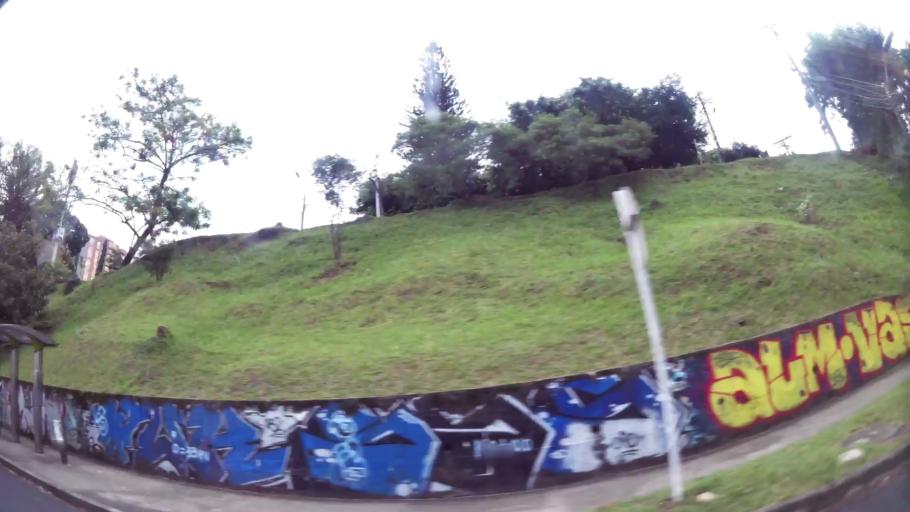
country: CO
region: Antioquia
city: Itagui
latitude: 6.1971
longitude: -75.5784
